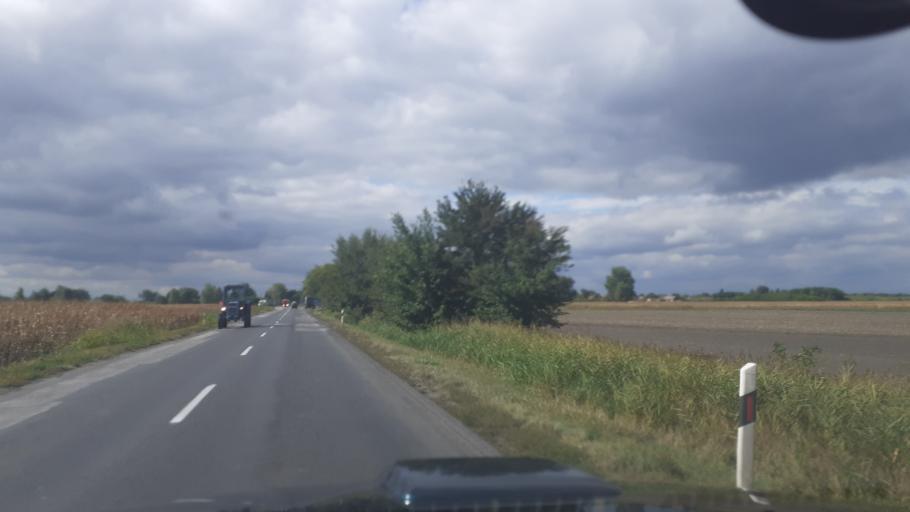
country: HU
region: Bacs-Kiskun
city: Solt
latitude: 46.7975
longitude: 19.0499
